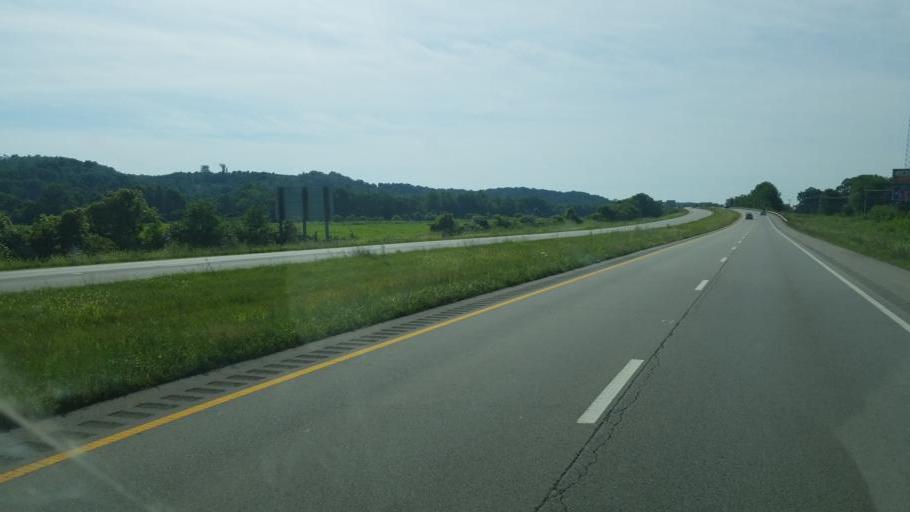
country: US
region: Ohio
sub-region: Hocking County
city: Logan
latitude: 39.4975
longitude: -82.3393
